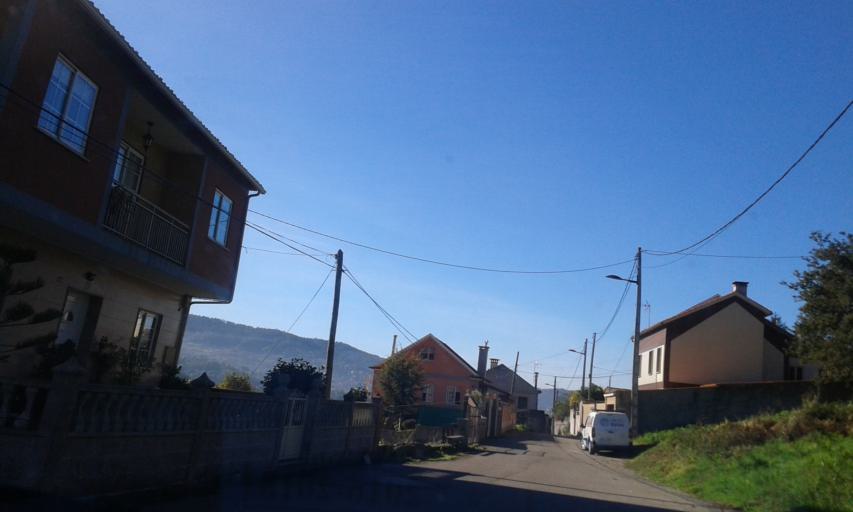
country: ES
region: Galicia
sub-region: Provincia de Pontevedra
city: Bueu
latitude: 42.3540
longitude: -8.7461
